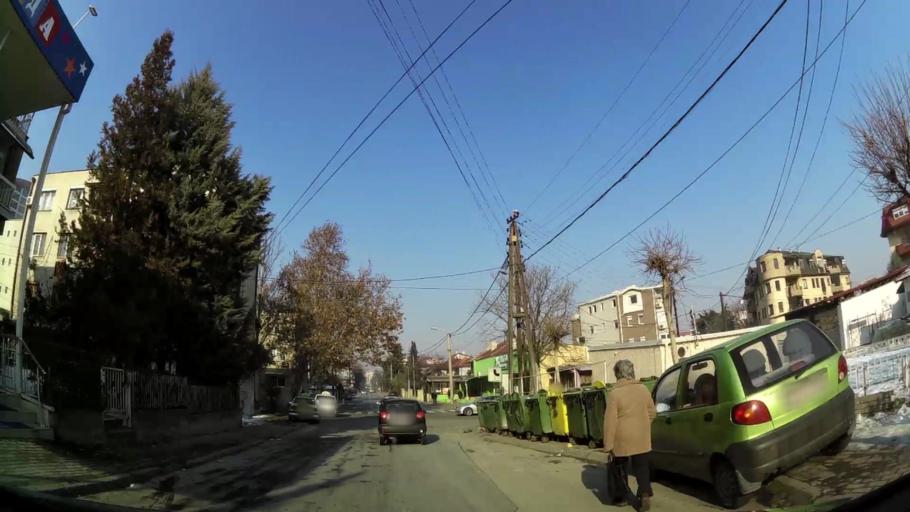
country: MK
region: Karpos
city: Skopje
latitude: 41.9757
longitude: 21.4384
